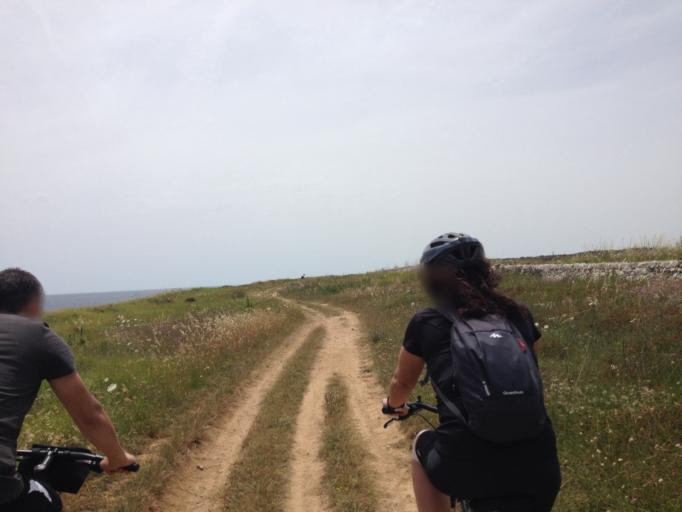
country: IT
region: Apulia
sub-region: Provincia di Lecce
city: Borgagne
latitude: 40.2626
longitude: 18.4428
